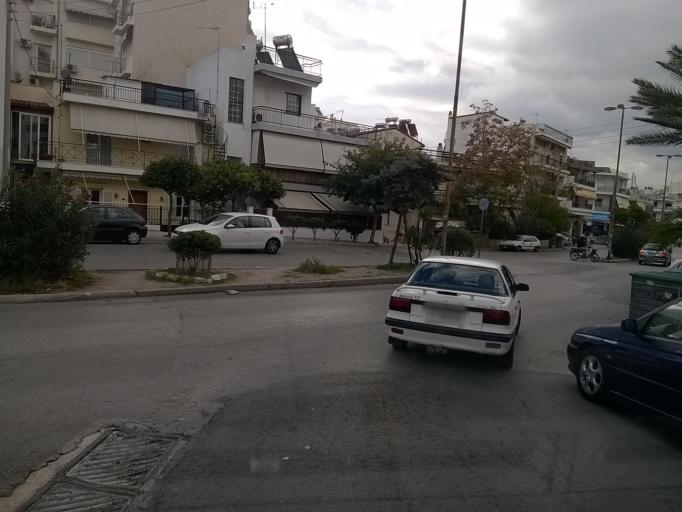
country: GR
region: Attica
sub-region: Nomarchia Athinas
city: Dhafni
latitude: 37.9443
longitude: 23.7287
